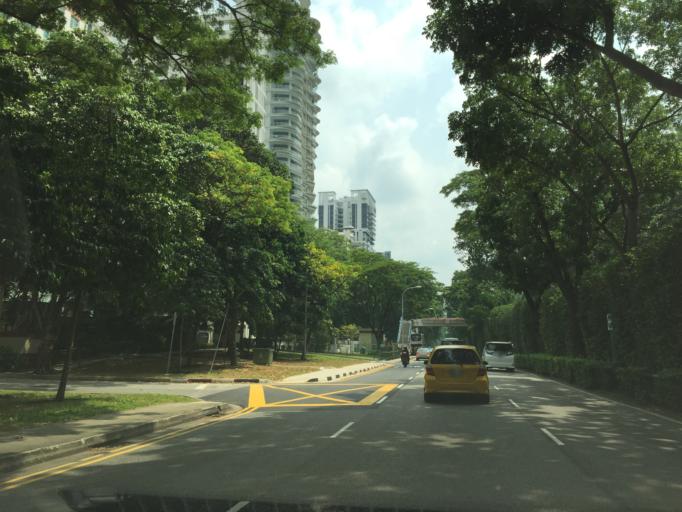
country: SG
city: Singapore
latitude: 1.3177
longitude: 103.8339
